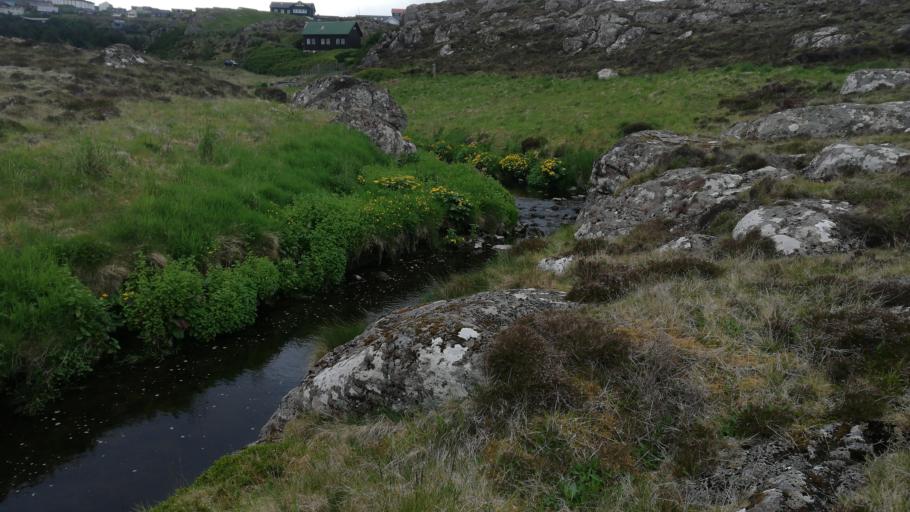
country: FO
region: Streymoy
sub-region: Torshavn
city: Torshavn
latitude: 62.0250
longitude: -6.7599
